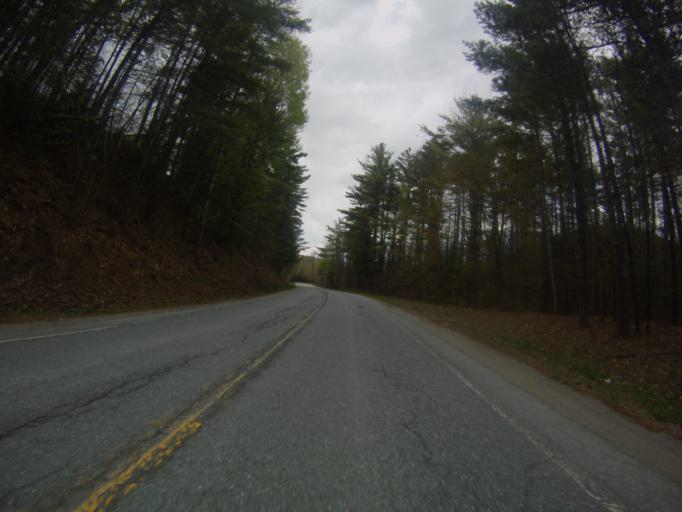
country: US
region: New York
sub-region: Essex County
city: Mineville
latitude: 44.0923
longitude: -73.5500
